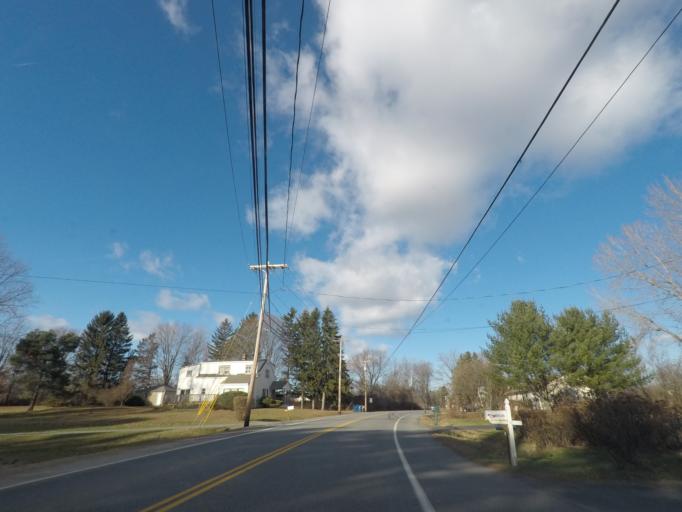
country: US
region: New York
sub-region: Saratoga County
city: Waterford
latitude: 42.8312
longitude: -73.7245
